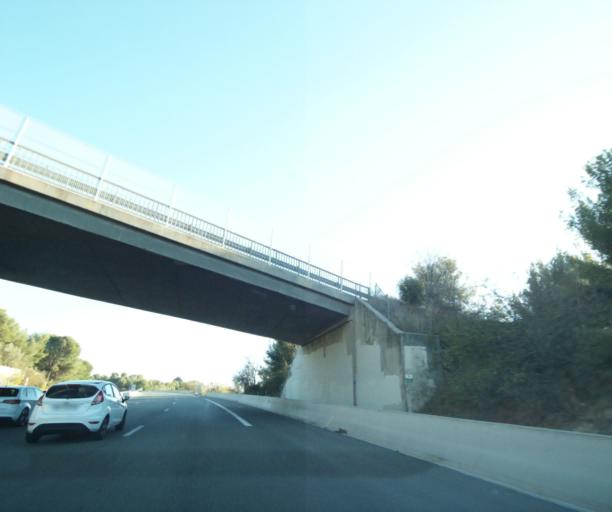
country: FR
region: Provence-Alpes-Cote d'Azur
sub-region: Departement des Bouches-du-Rhone
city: Ceyreste
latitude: 43.2029
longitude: 5.6326
